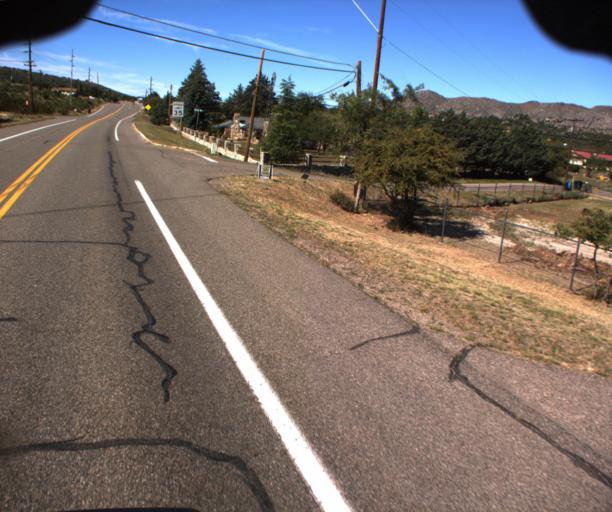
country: US
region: Arizona
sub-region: Yavapai County
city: Congress
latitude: 34.2290
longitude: -112.7408
